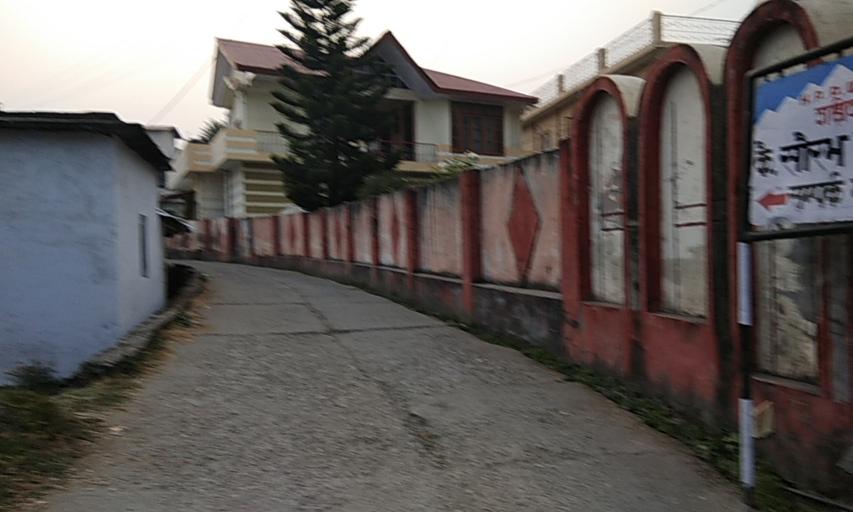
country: IN
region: Himachal Pradesh
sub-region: Kangra
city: Palampur
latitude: 32.1168
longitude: 76.5326
